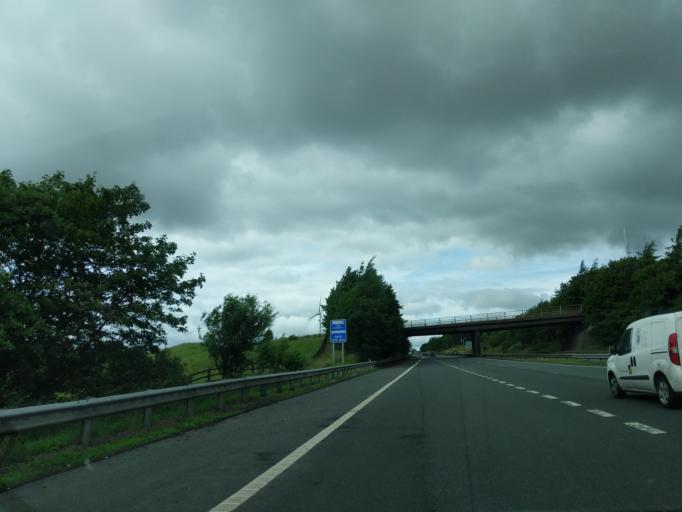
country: GB
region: Scotland
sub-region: South Lanarkshire
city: Douglas
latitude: 55.5975
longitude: -3.8349
